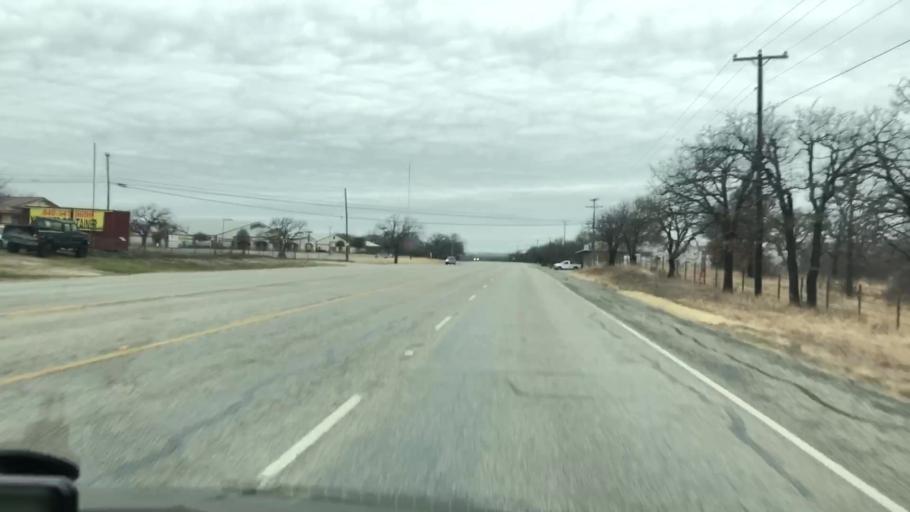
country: US
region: Texas
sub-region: Jack County
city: Jacksboro
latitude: 33.2277
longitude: -98.1734
